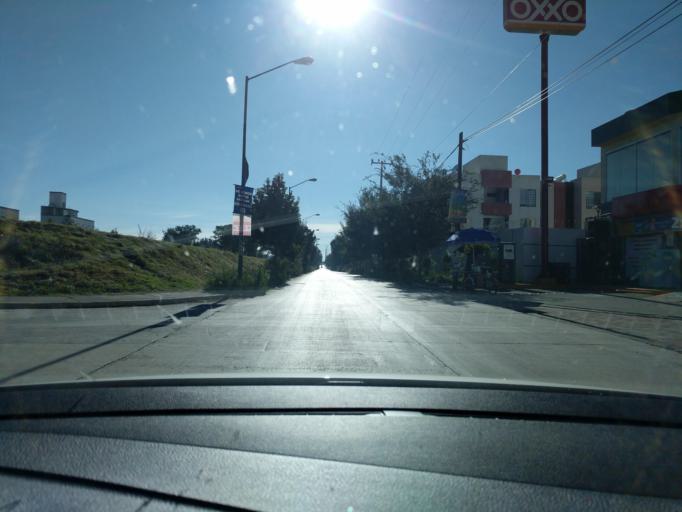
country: MX
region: Puebla
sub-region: Huejotzingo
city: Los Encinos
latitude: 19.1756
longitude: -98.3881
